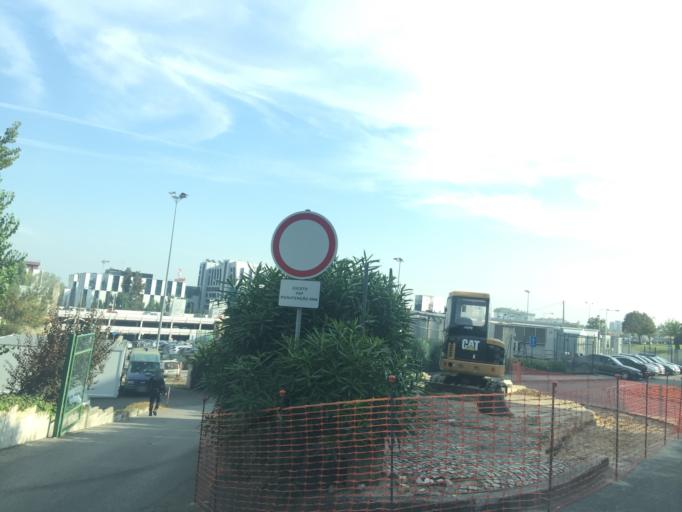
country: PT
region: Lisbon
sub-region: Loures
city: Moscavide
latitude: 38.7716
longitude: -9.1282
